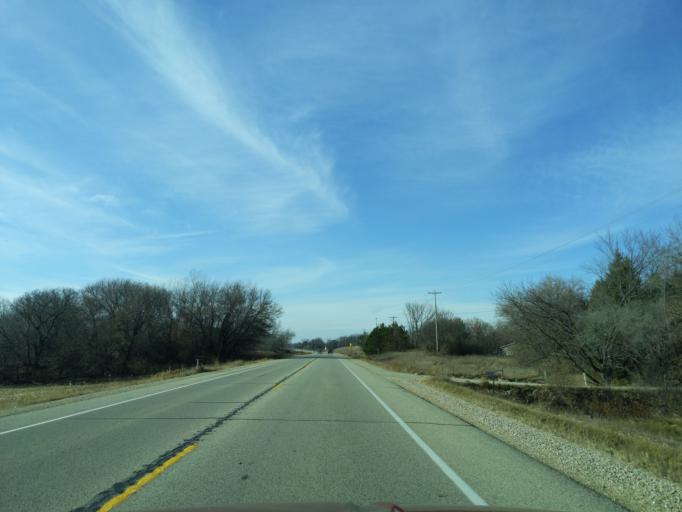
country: US
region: Wisconsin
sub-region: Walworth County
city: Whitewater
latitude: 42.8065
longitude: -88.6629
